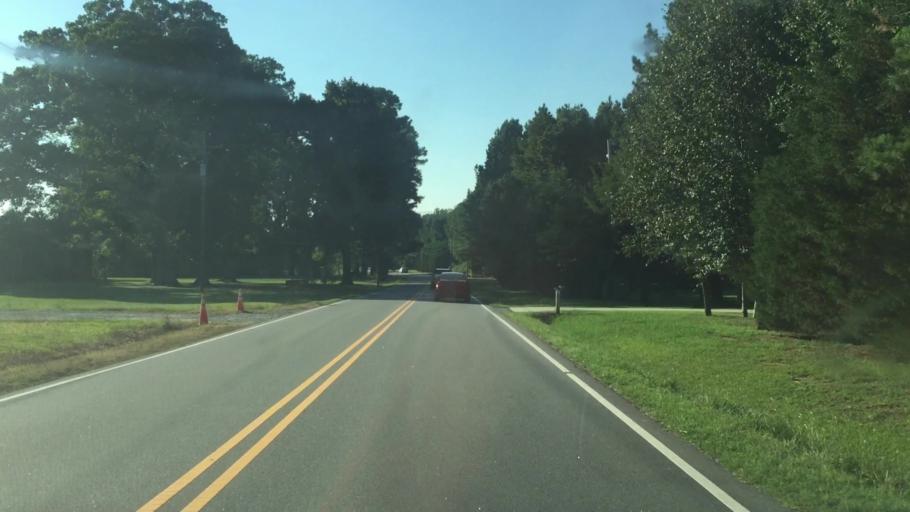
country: US
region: North Carolina
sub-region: Rowan County
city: Enochville
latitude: 35.4727
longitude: -80.7457
